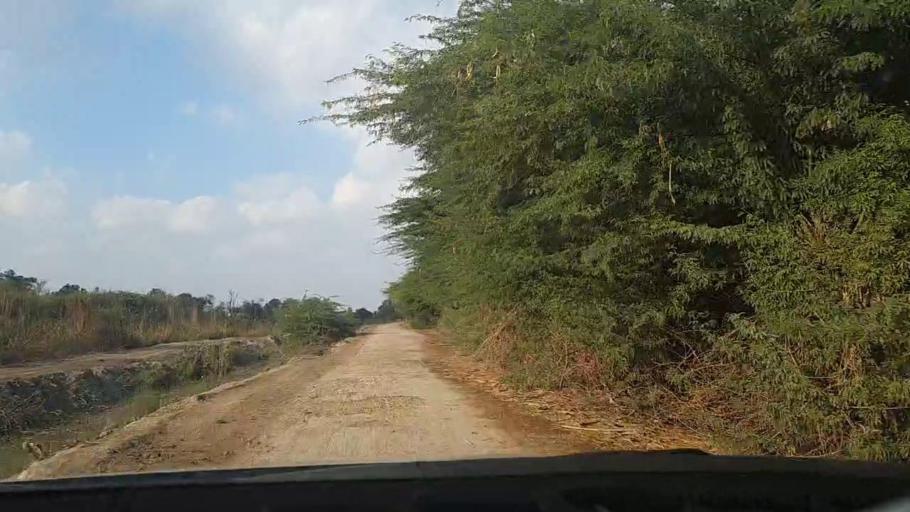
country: PK
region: Sindh
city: Tando Mittha Khan
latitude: 25.9144
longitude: 69.3039
